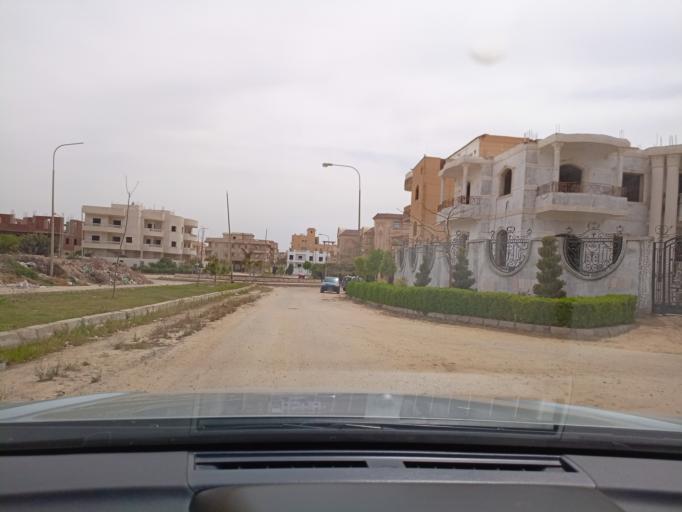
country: EG
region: Muhafazat al Qalyubiyah
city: Al Khankah
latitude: 30.2478
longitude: 31.5045
